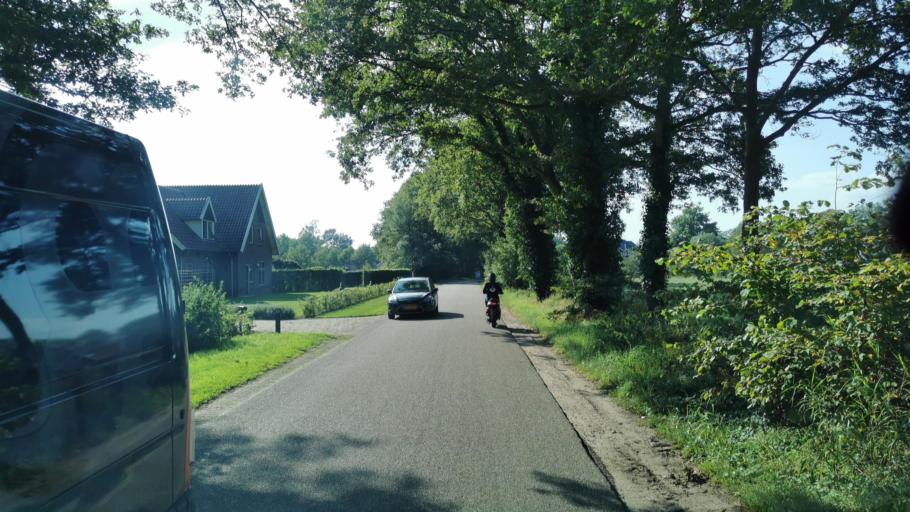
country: NL
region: Overijssel
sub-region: Gemeente Borne
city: Borne
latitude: 52.3364
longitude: 6.8000
